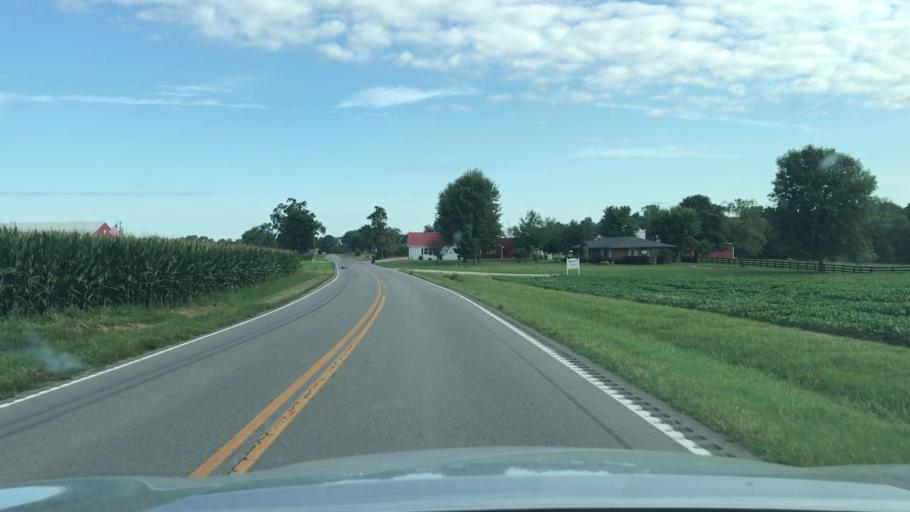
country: US
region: Kentucky
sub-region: Todd County
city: Elkton
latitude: 36.8580
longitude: -87.1589
